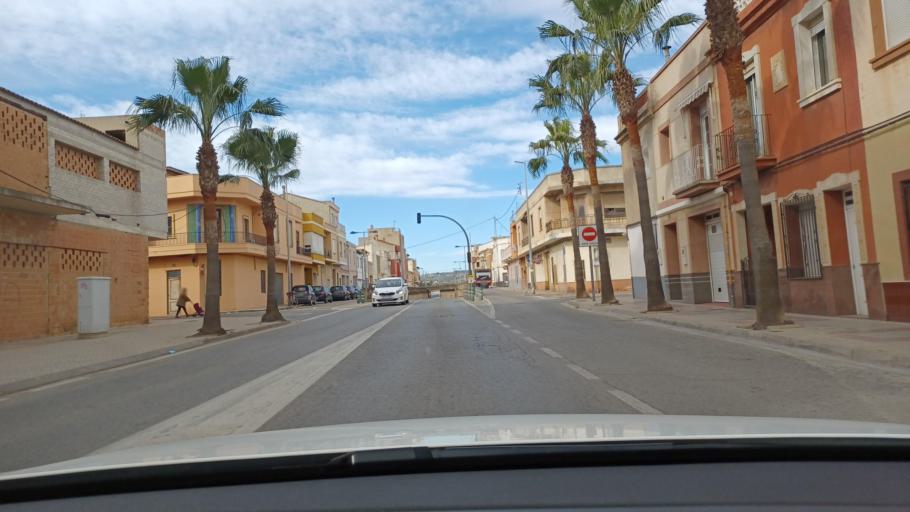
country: ES
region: Valencia
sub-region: Provincia de Valencia
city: Benifaio
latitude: 39.2887
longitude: -0.4268
